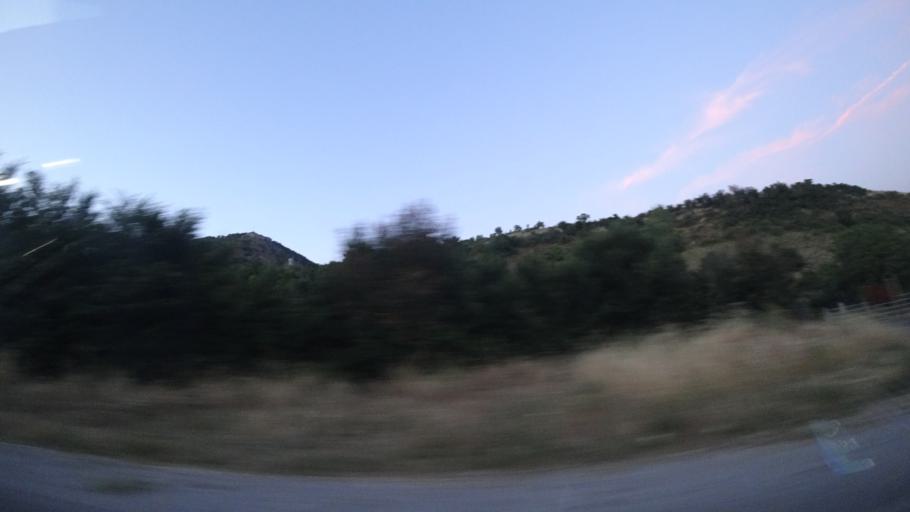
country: FR
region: Midi-Pyrenees
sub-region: Departement de l'Aveyron
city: Millau
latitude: 44.1268
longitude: 3.0559
